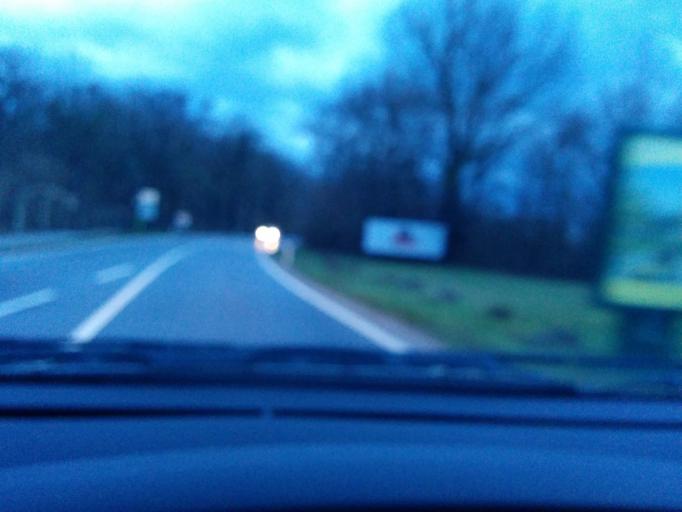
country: AT
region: Lower Austria
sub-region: Politischer Bezirk Modling
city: Laxenburg
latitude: 48.0637
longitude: 16.3532
